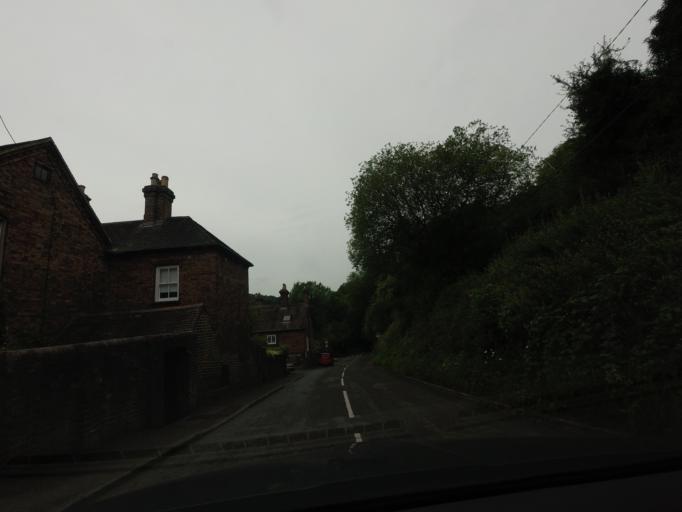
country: GB
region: England
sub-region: Telford and Wrekin
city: Ironbridge
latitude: 52.6420
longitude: -2.4873
